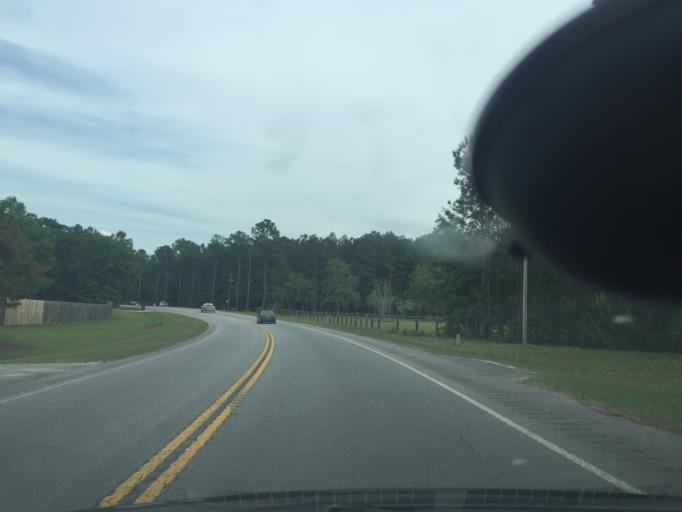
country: US
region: Georgia
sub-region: Bryan County
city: Richmond Hill
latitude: 32.0174
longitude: -81.3099
